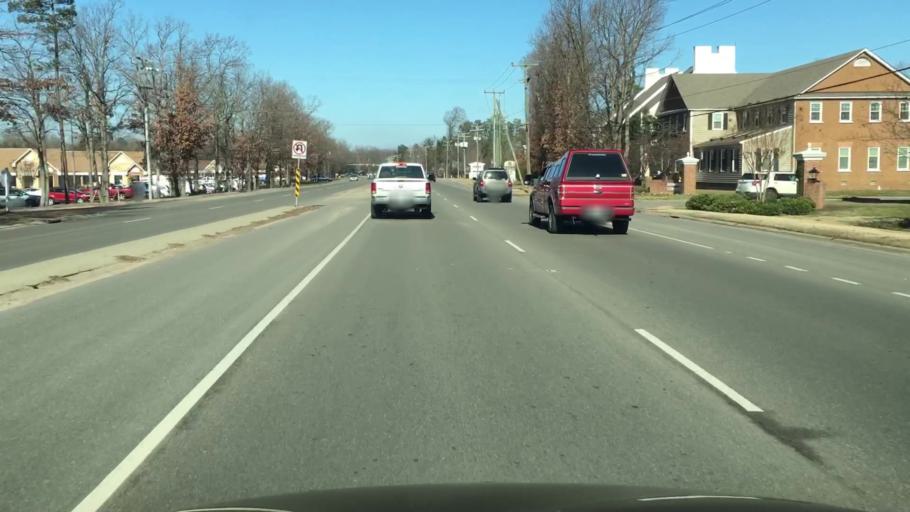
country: US
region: Virginia
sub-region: Chesterfield County
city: Bon Air
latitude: 37.5133
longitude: -77.6148
